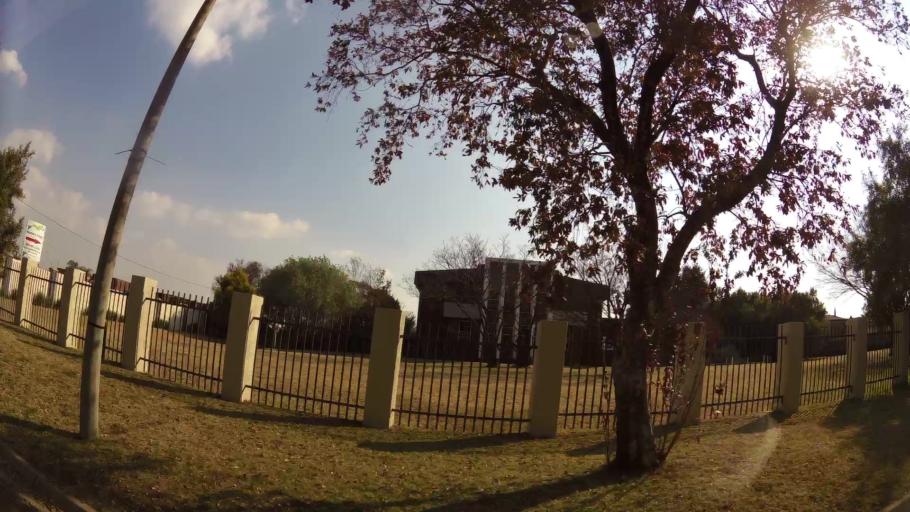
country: ZA
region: Gauteng
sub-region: Ekurhuleni Metropolitan Municipality
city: Boksburg
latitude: -26.1852
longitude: 28.2633
